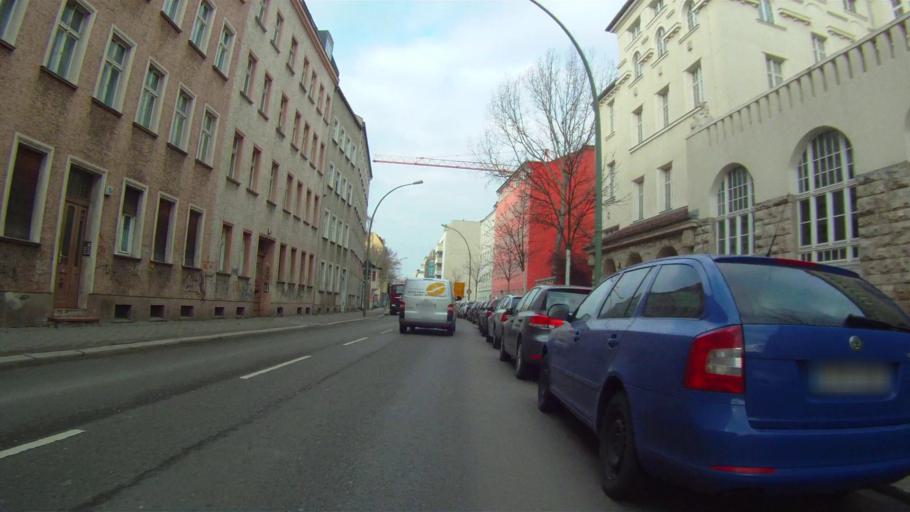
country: DE
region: Berlin
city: Rummelsburg
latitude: 52.5018
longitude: 13.4896
